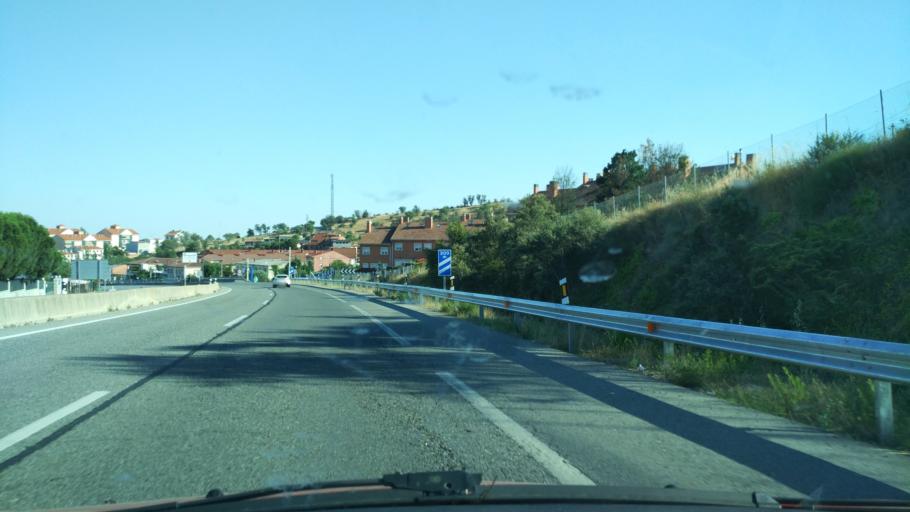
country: ES
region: Madrid
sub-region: Provincia de Madrid
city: El Molar
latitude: 40.7342
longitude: -3.5859
